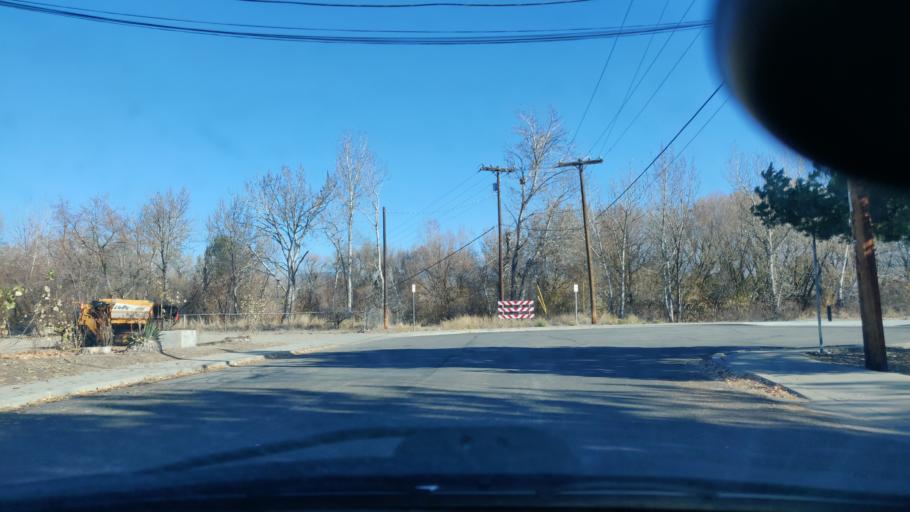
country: US
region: Idaho
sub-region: Ada County
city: Garden City
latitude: 43.6383
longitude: -116.2454
